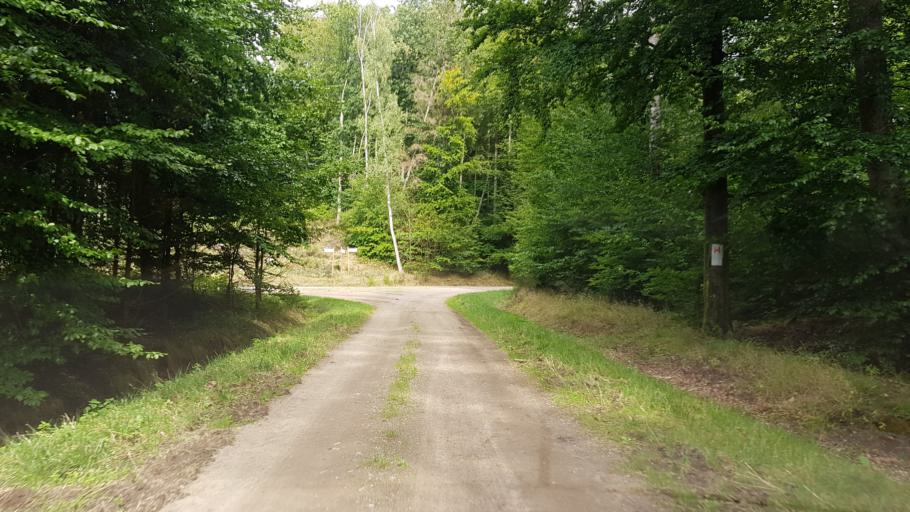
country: PL
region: West Pomeranian Voivodeship
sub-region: Powiat bialogardzki
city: Tychowo
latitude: 53.9754
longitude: 16.3806
